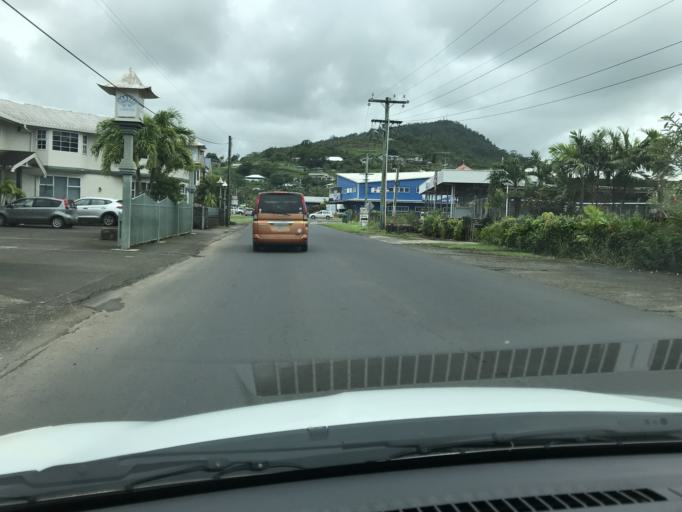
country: WS
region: Tuamasaga
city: Apia
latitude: -13.8361
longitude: -171.7680
